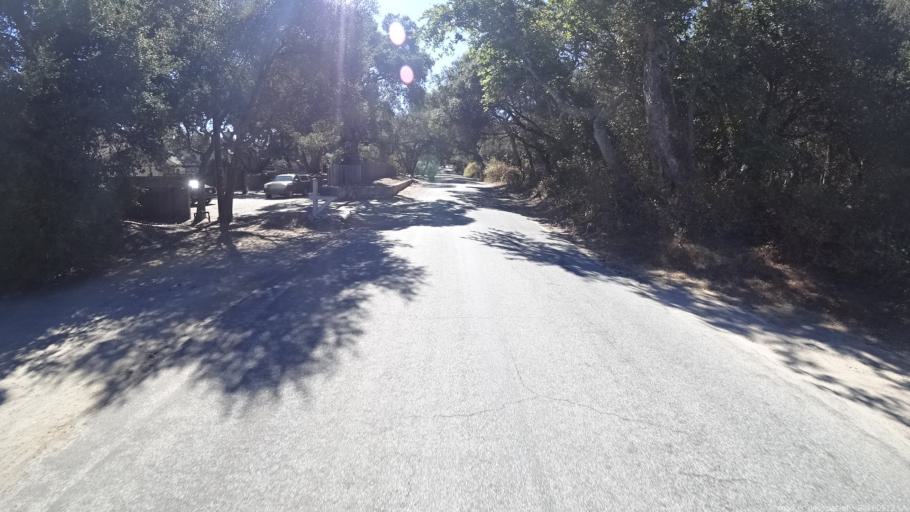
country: US
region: California
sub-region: Monterey County
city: Carmel Valley Village
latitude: 36.4882
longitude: -121.7493
